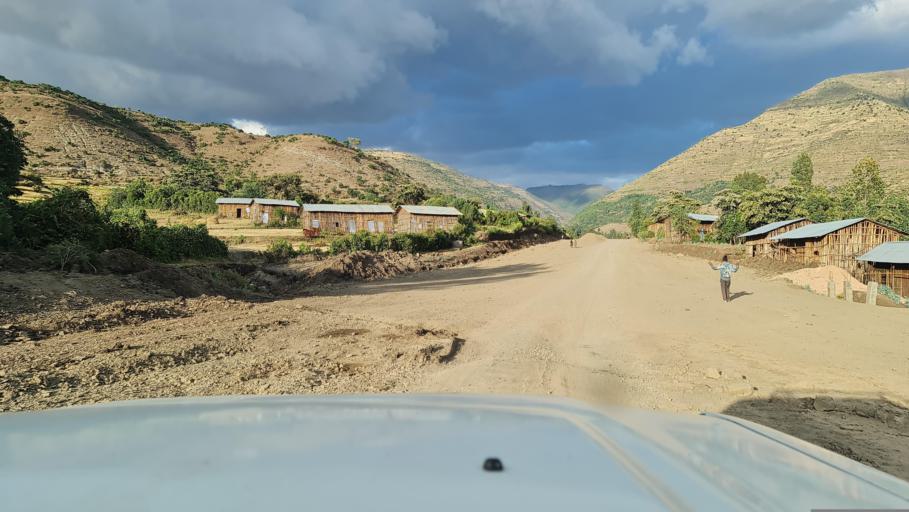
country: ET
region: Amhara
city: Debark'
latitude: 13.0379
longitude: 38.0489
